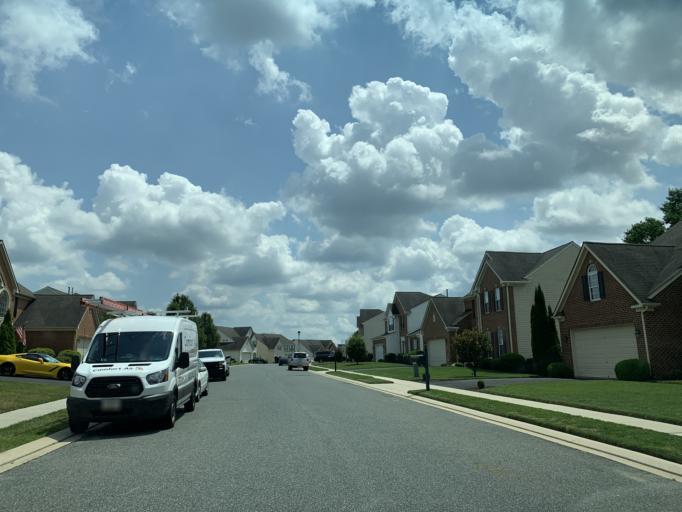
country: US
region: Maryland
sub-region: Harford County
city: Bel Air North
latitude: 39.5593
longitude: -76.3592
